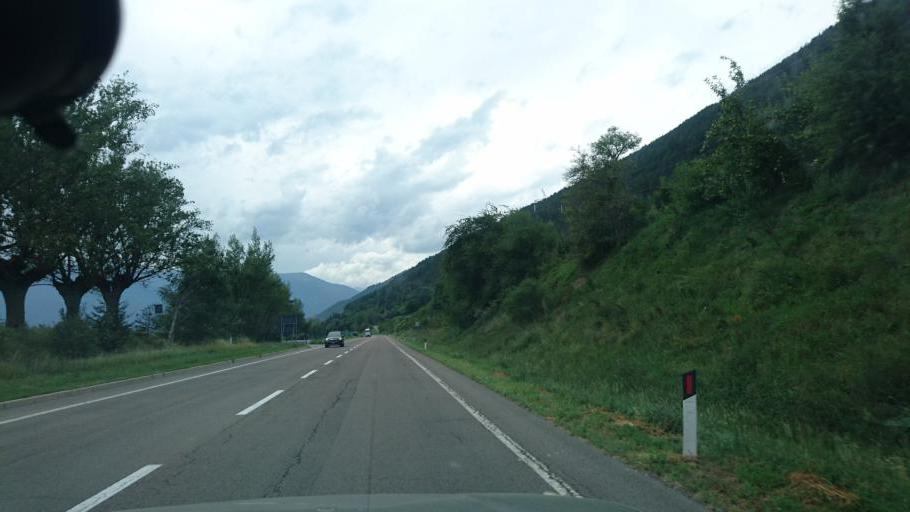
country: IT
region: Trentino-Alto Adige
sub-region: Bolzano
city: Lasa
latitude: 46.6269
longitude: 10.6828
